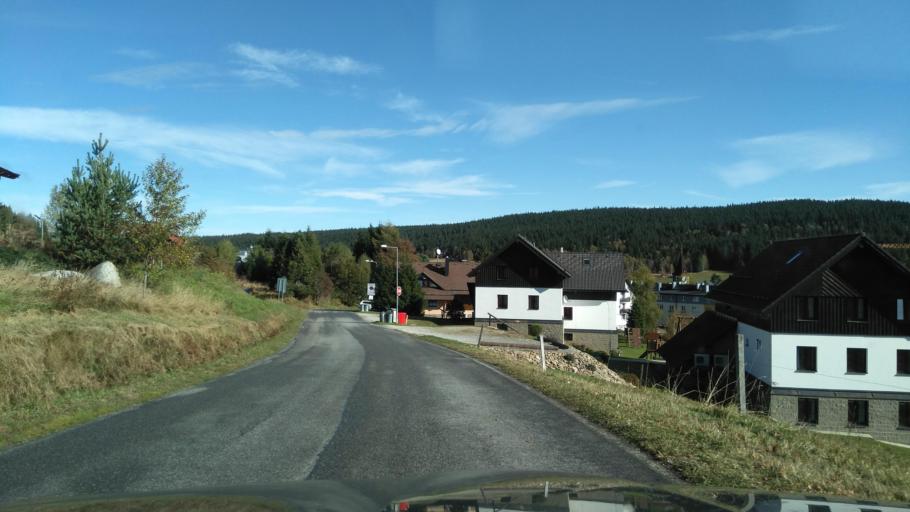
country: CZ
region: Jihocesky
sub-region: Okres Prachatice
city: Borova Lada
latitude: 49.0176
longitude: 13.5763
